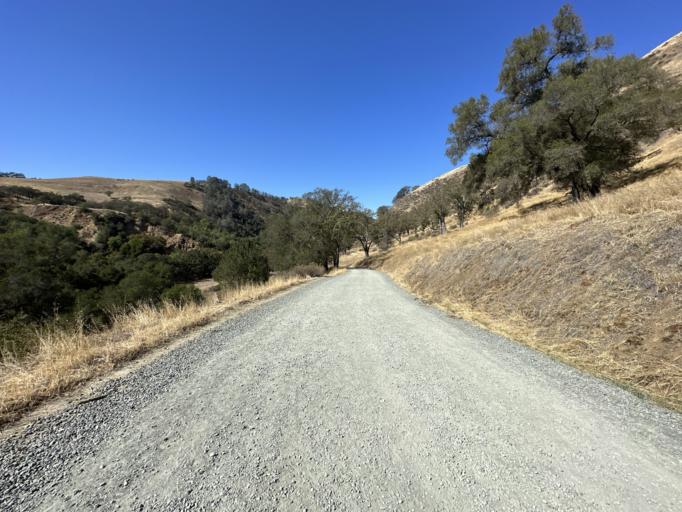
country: US
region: California
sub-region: Santa Clara County
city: Milpitas
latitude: 37.5039
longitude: -121.8216
